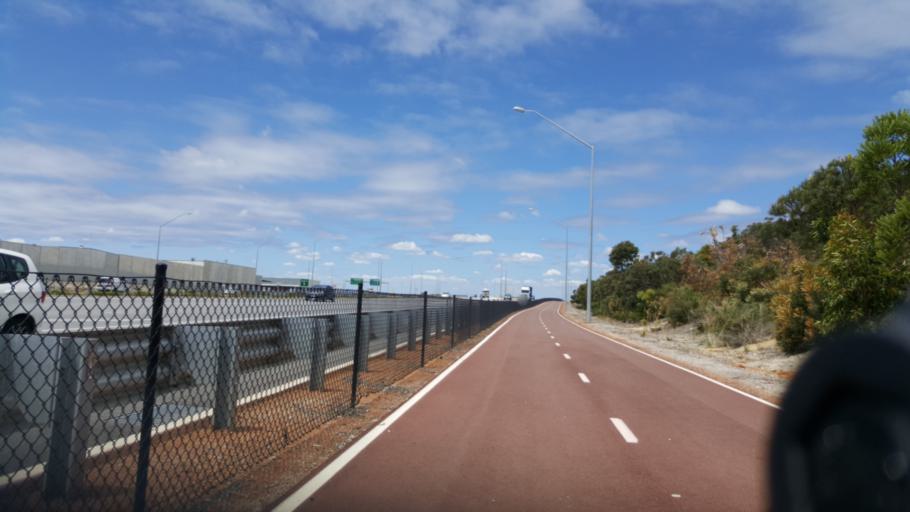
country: AU
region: Western Australia
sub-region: Bayswater
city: Embleton
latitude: -31.8663
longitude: 115.9082
